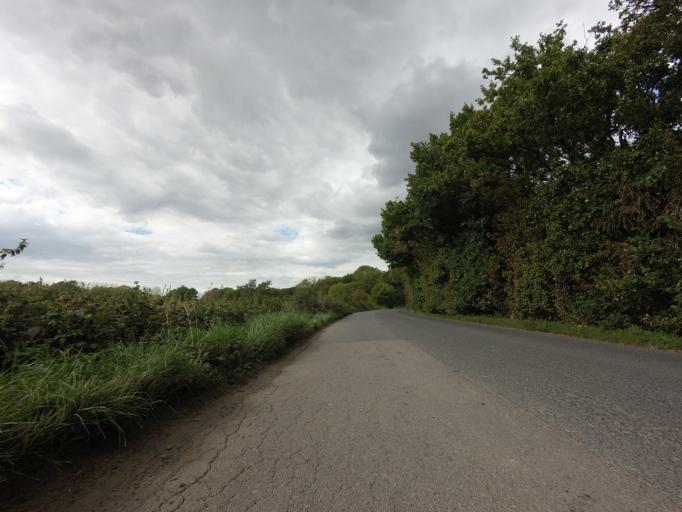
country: GB
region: England
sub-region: Kent
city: Paddock Wood
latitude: 51.1690
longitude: 0.4192
